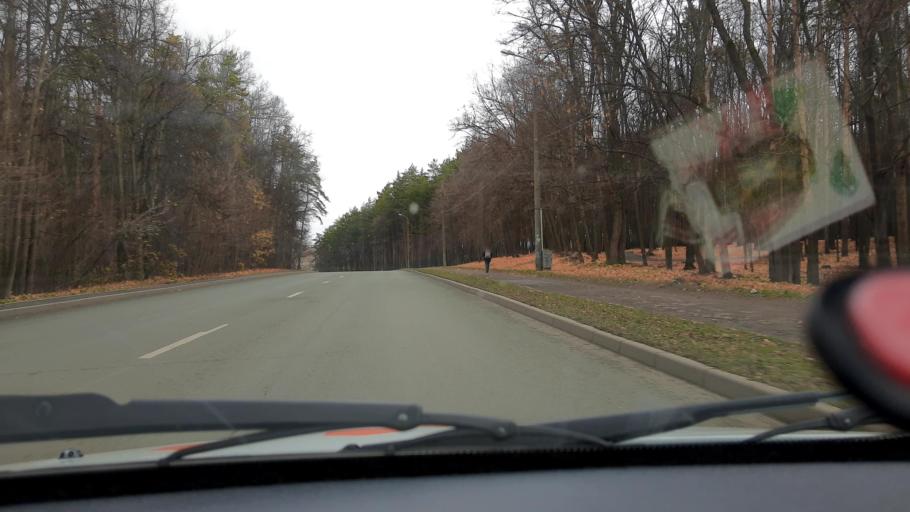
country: RU
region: Bashkortostan
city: Ufa
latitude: 54.7837
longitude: 56.0272
